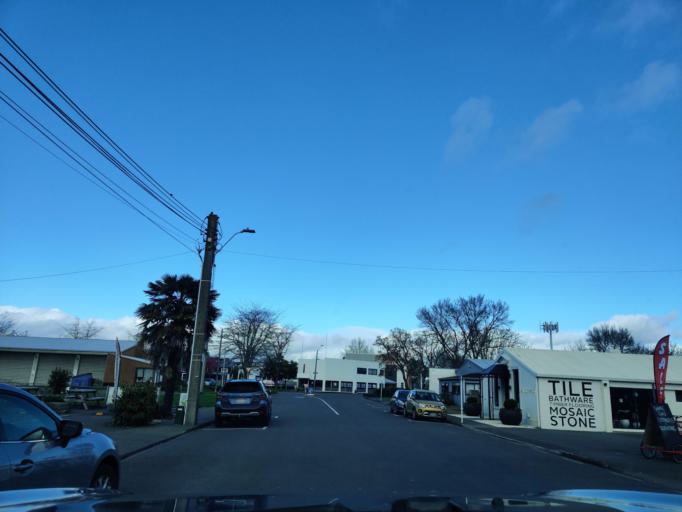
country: NZ
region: Hawke's Bay
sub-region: Hastings District
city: Hastings
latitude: -39.6678
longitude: 176.8778
